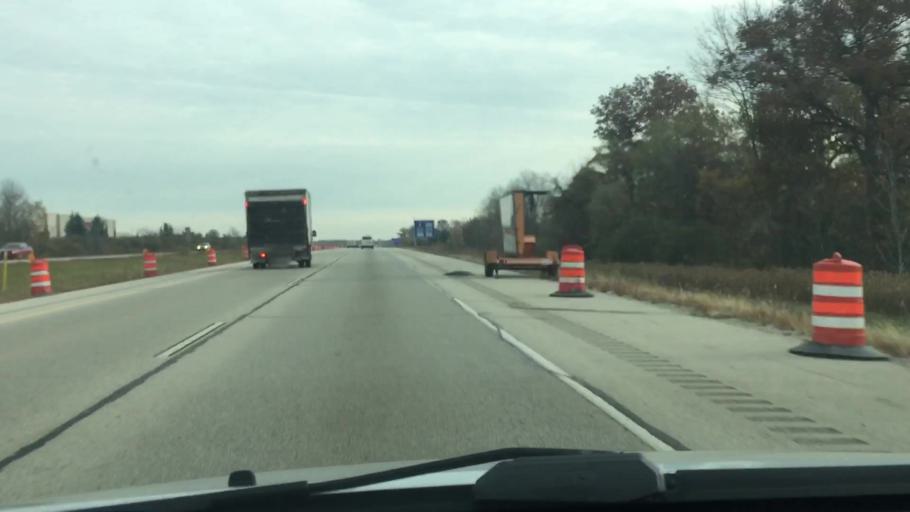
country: US
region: Wisconsin
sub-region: Waukesha County
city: New Berlin
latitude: 42.9438
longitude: -88.1224
